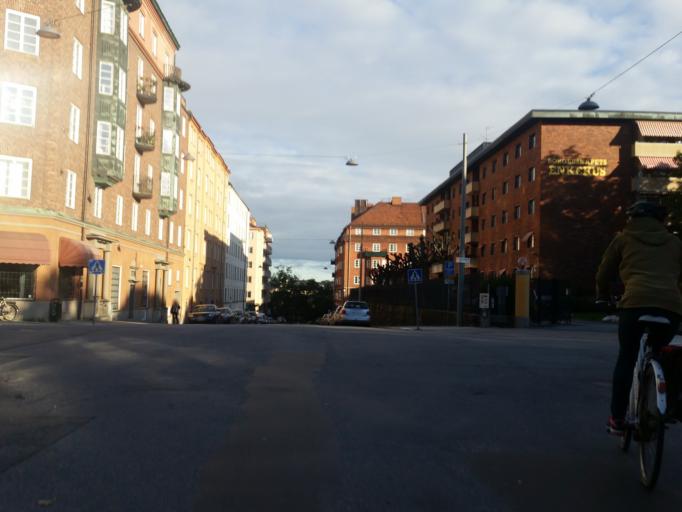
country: SE
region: Stockholm
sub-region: Stockholms Kommun
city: Arsta
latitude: 59.3182
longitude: 18.0399
